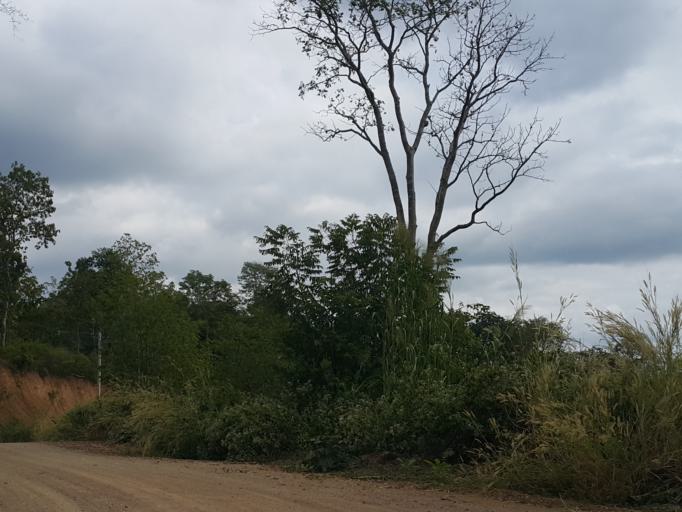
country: TH
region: Lampang
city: Chae Hom
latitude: 18.5774
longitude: 99.4400
